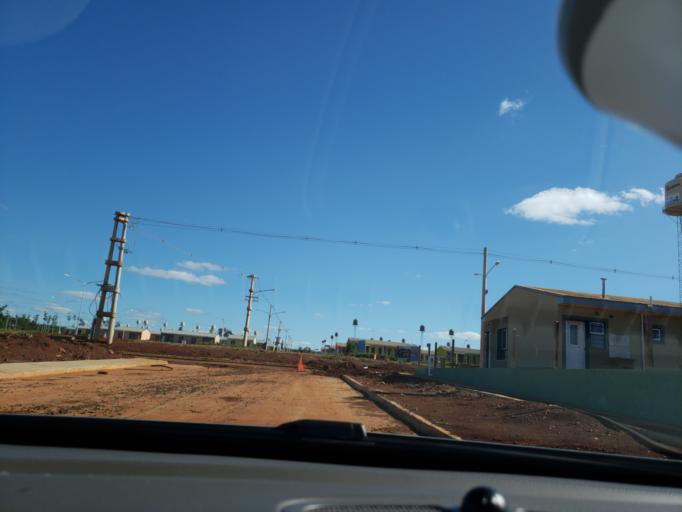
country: AR
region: Misiones
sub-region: Departamento de Capital
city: Posadas
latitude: -27.4137
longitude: -55.9891
